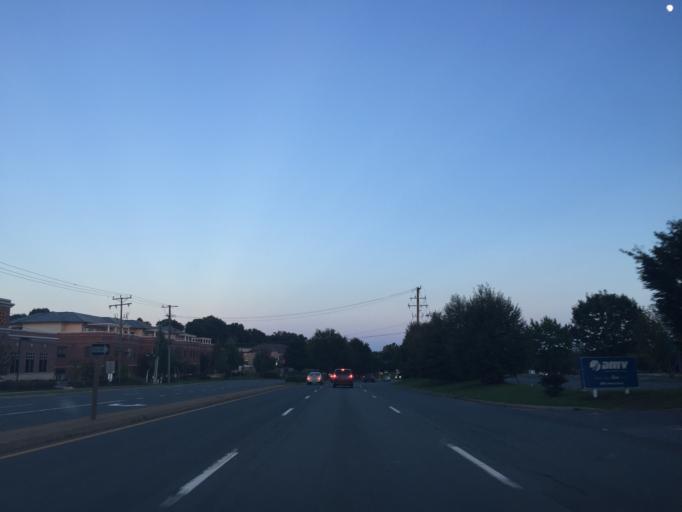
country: US
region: Virginia
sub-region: City of Charlottesville
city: Charlottesville
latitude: 38.0300
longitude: -78.4431
